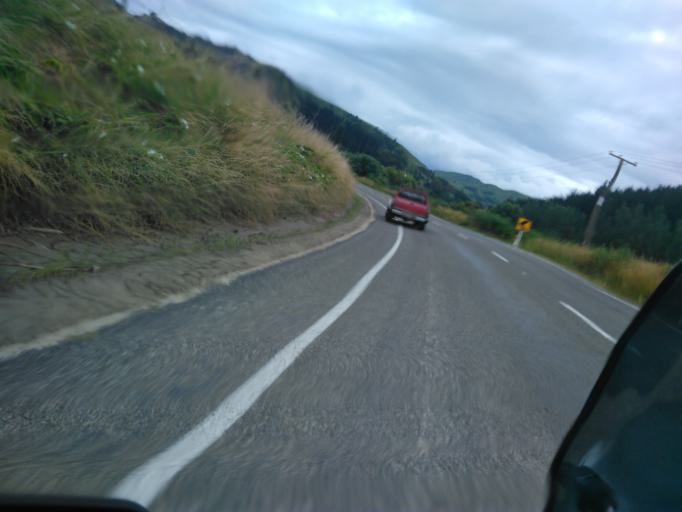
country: NZ
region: Gisborne
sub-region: Gisborne District
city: Gisborne
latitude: -38.4603
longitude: 177.7455
